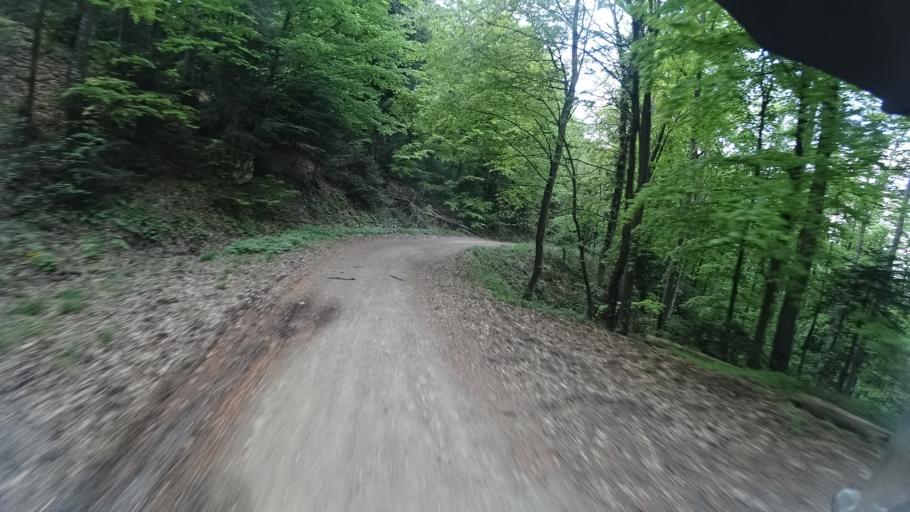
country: HR
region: Grad Zagreb
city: Kasina
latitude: 45.9383
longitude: 16.0334
